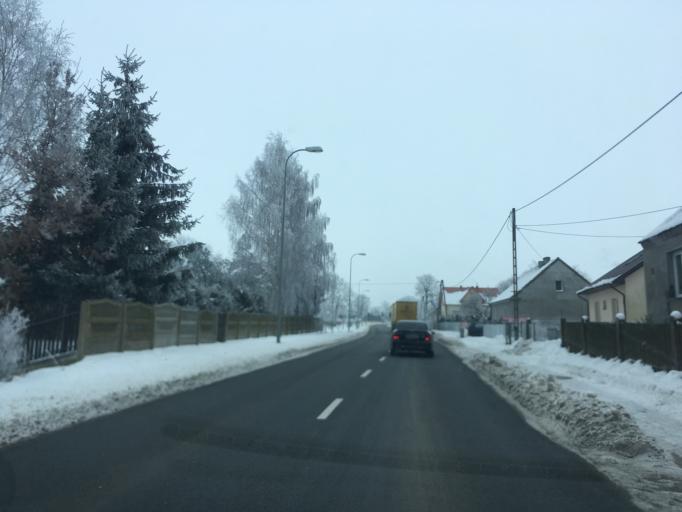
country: PL
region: Warmian-Masurian Voivodeship
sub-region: Powiat dzialdowski
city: Dzialdowo
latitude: 53.2341
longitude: 20.0940
